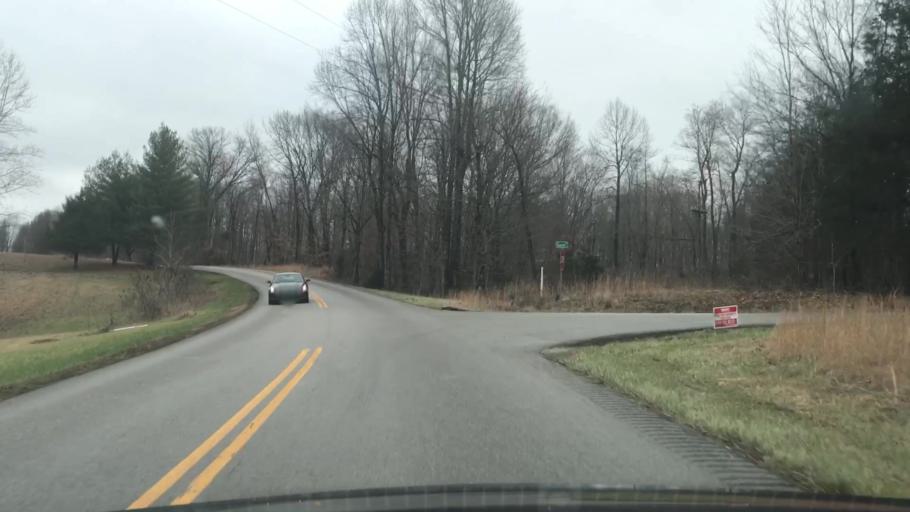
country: US
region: Kentucky
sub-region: Barren County
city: Glasgow
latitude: 36.8829
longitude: -85.7917
